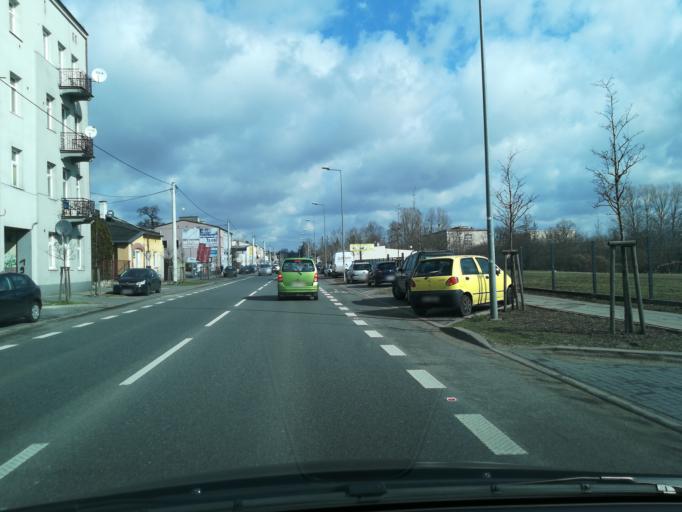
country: PL
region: Silesian Voivodeship
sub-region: Czestochowa
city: Czestochowa
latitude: 50.8213
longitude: 19.1321
